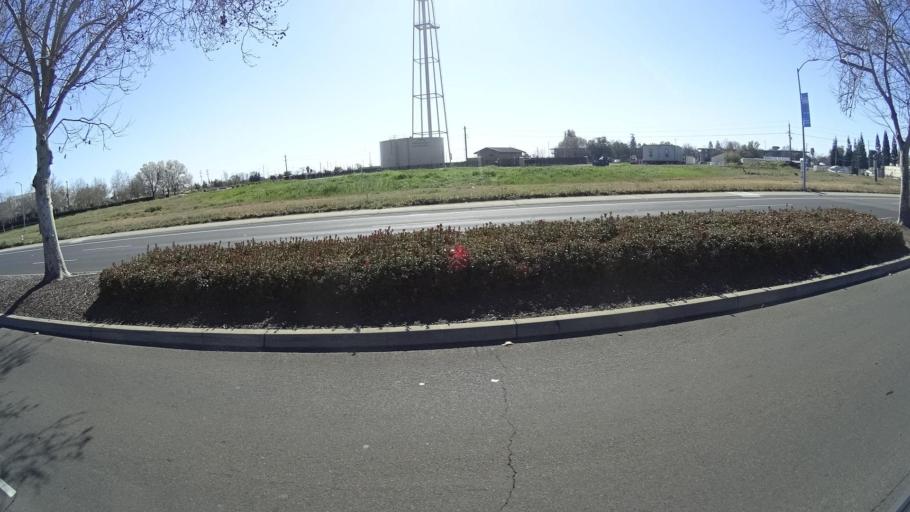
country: US
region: California
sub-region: Sacramento County
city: Rancho Cordova
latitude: 38.5752
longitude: -121.2933
